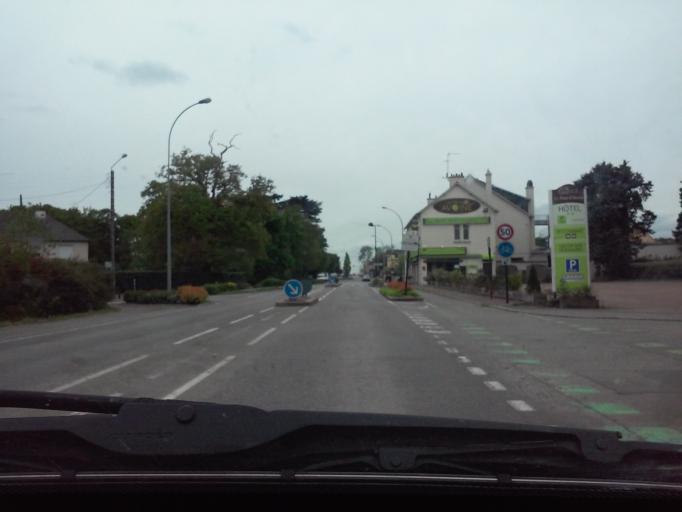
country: FR
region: Brittany
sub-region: Departement d'Ille-et-Vilaine
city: Vezin-le-Coquet
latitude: 48.0967
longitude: -1.7624
